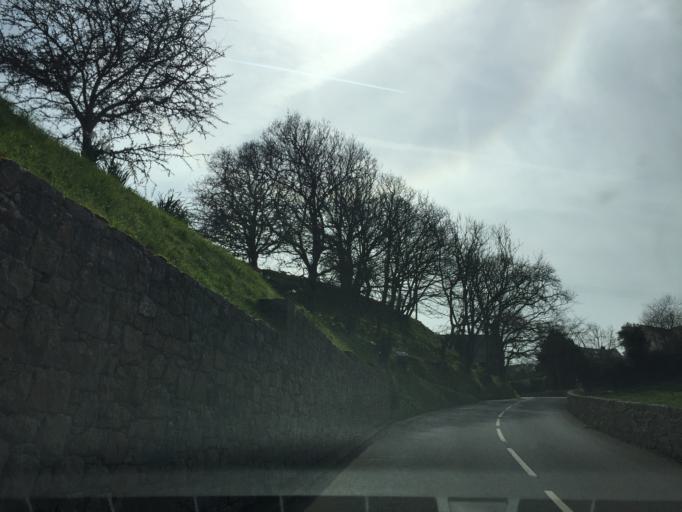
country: JE
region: St Helier
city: Saint Helier
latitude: 49.2419
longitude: -2.2039
